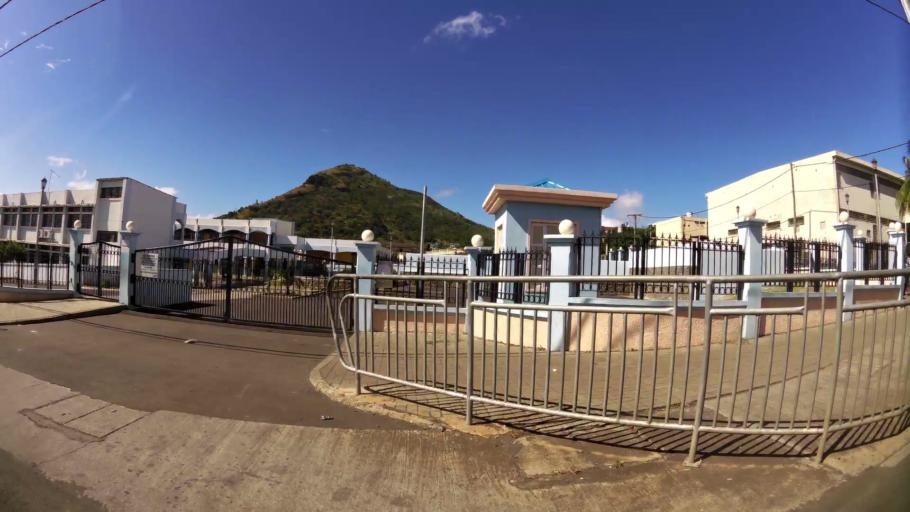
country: MU
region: Black River
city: Cascavelle
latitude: -20.2658
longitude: 57.4163
